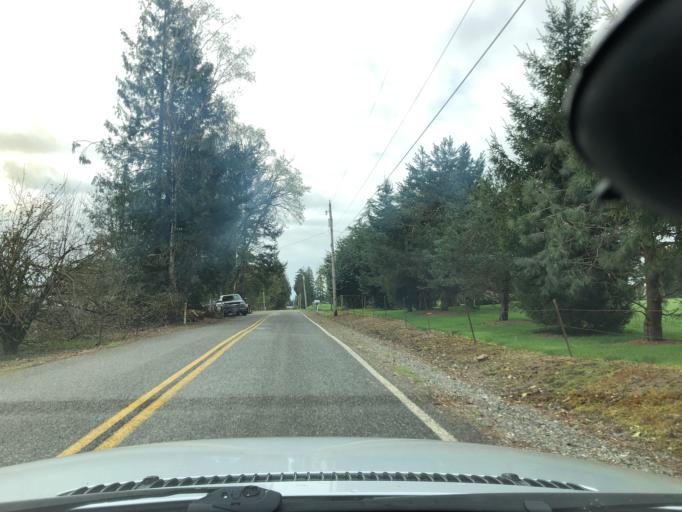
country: US
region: Washington
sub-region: Whatcom County
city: Lynden
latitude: 48.9911
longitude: -122.5184
